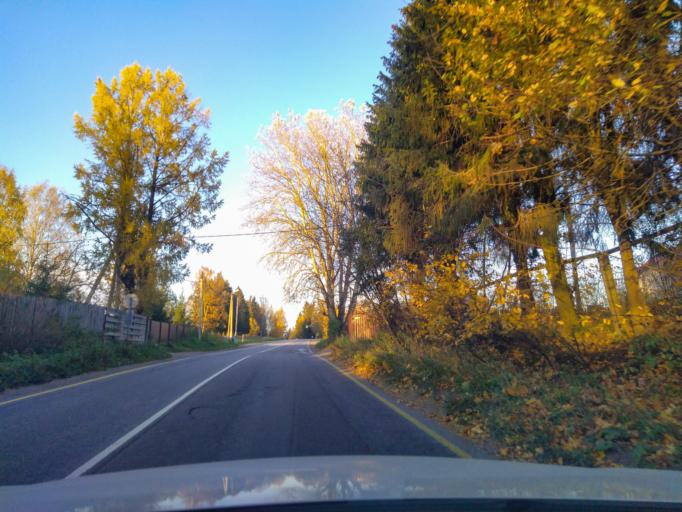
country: RU
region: Leningrad
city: Kobrinskoye
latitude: 59.4493
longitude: 30.1086
